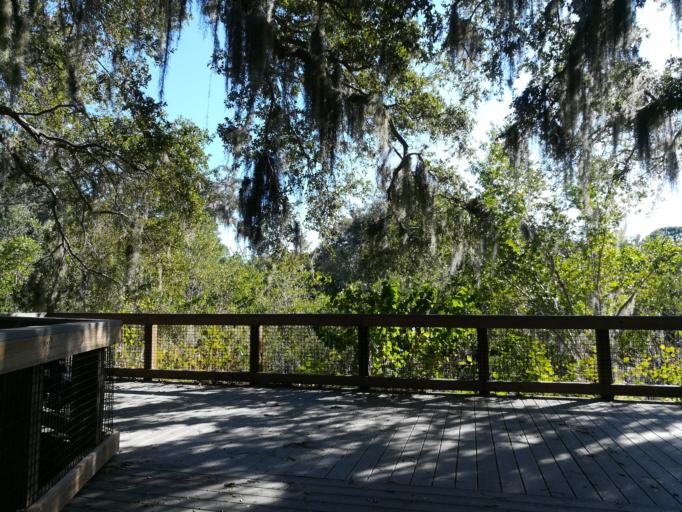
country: US
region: Florida
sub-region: Pinellas County
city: North Redington Beach
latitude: 27.8313
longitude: -82.8093
